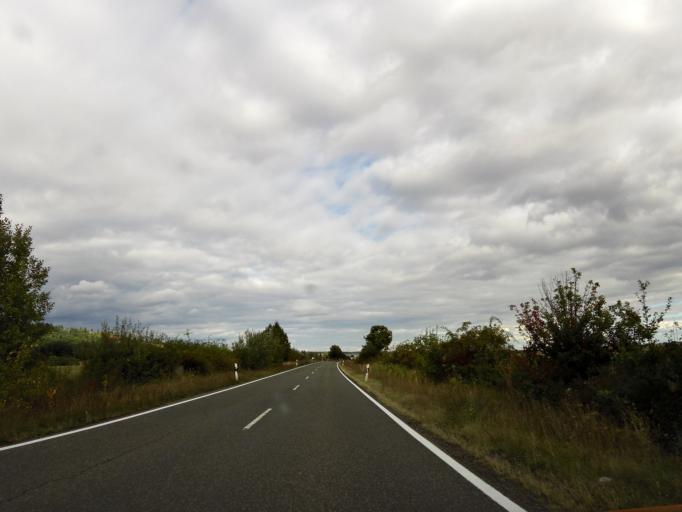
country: DE
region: Rheinland-Pfalz
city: Bolanden
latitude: 49.6471
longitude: 7.9951
